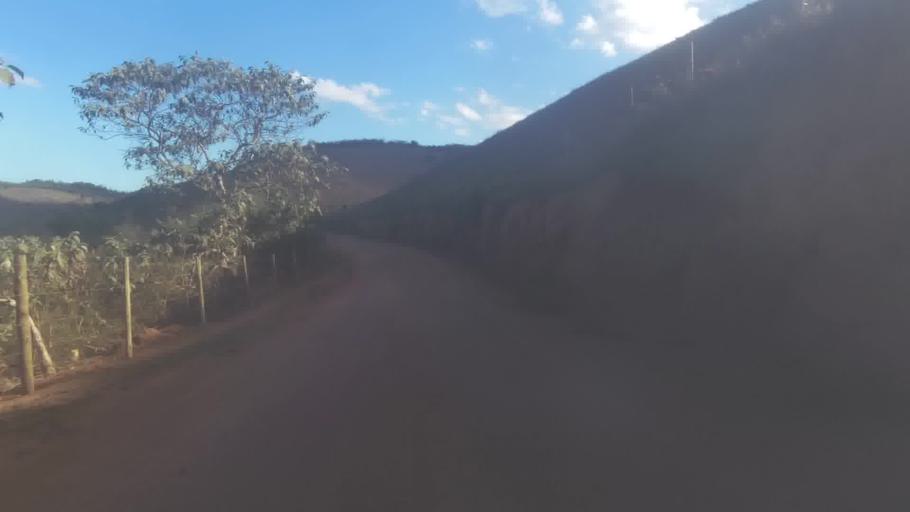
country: BR
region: Espirito Santo
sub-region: Mimoso Do Sul
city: Mimoso do Sul
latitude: -21.0766
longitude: -41.1455
